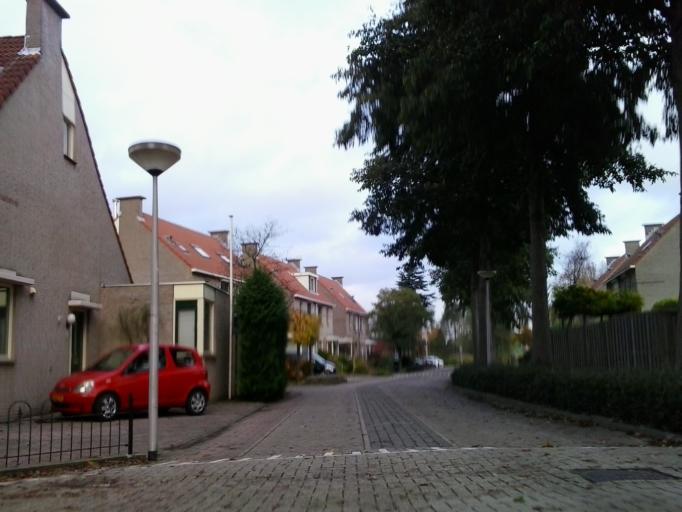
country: NL
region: South Holland
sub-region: Gemeente Lansingerland
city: Berkel en Rodenrijs
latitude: 51.9903
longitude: 4.4700
